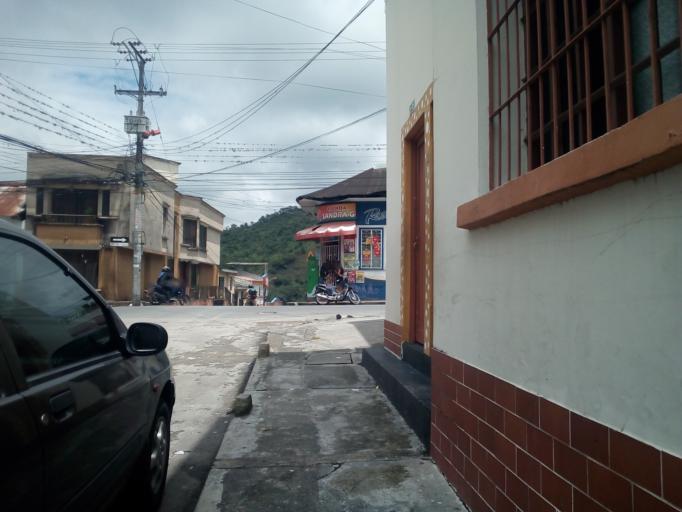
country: CO
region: Tolima
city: Ibague
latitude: 4.4477
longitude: -75.2464
